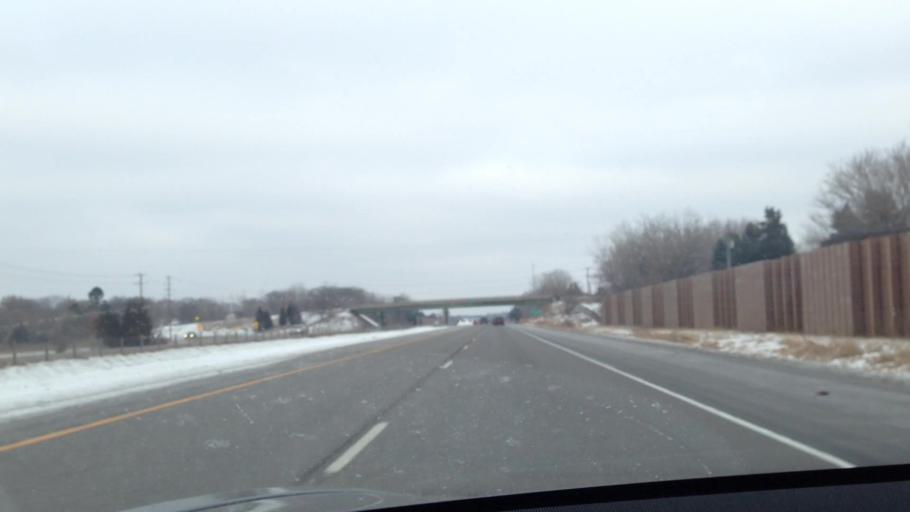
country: US
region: Minnesota
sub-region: Anoka County
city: Circle Pines
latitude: 45.1672
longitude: -93.1462
